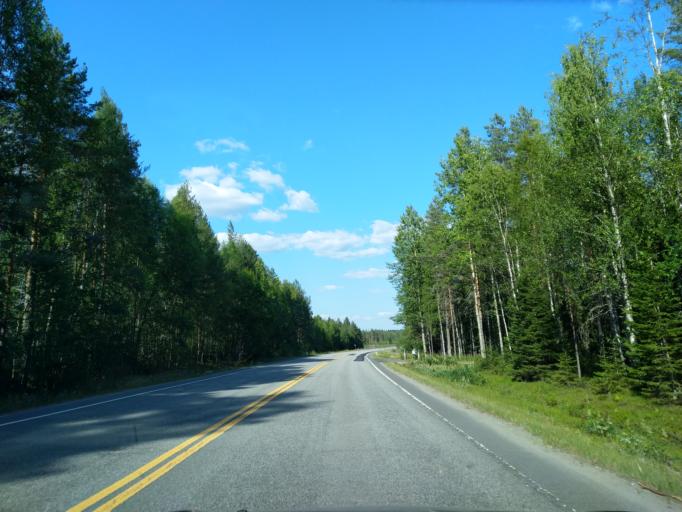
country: FI
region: Pirkanmaa
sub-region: Luoteis-Pirkanmaa
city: Kihnioe
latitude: 62.1267
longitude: 23.1158
